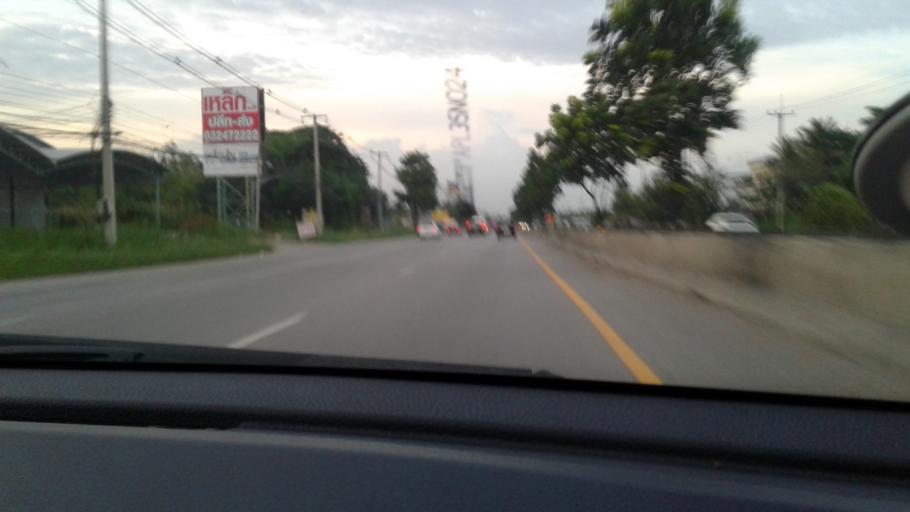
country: TH
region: Phetchaburi
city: Cha-am
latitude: 12.8547
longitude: 99.9242
